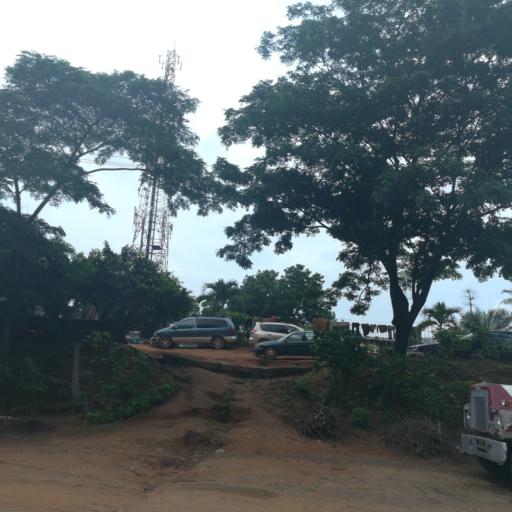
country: NG
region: Lagos
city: Ojota
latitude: 6.6069
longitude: 3.3725
